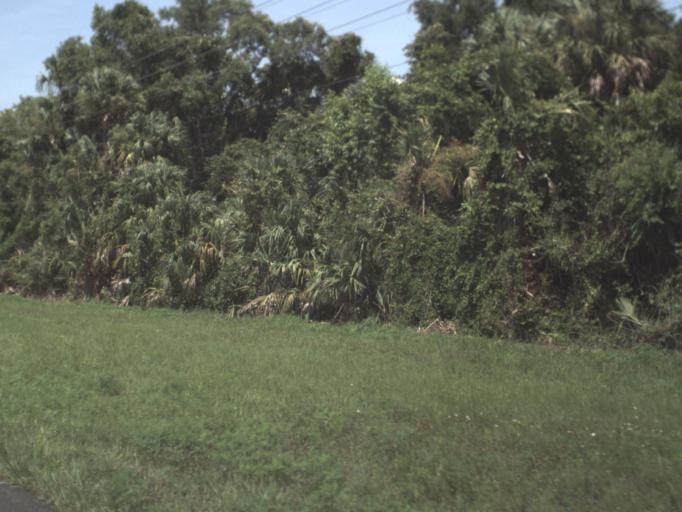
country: US
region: Florida
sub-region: Levy County
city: Inglis
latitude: 29.0241
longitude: -82.6691
